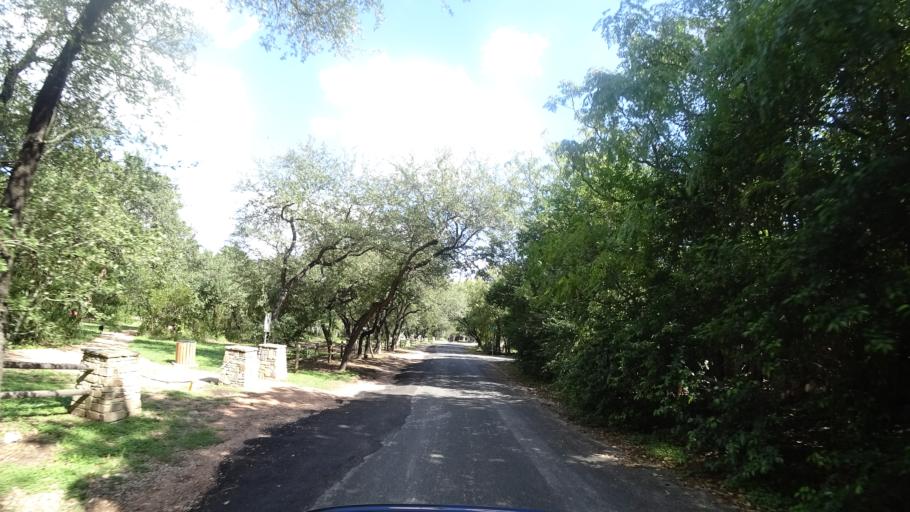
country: US
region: Texas
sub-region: Travis County
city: Onion Creek
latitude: 30.1999
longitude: -97.7918
